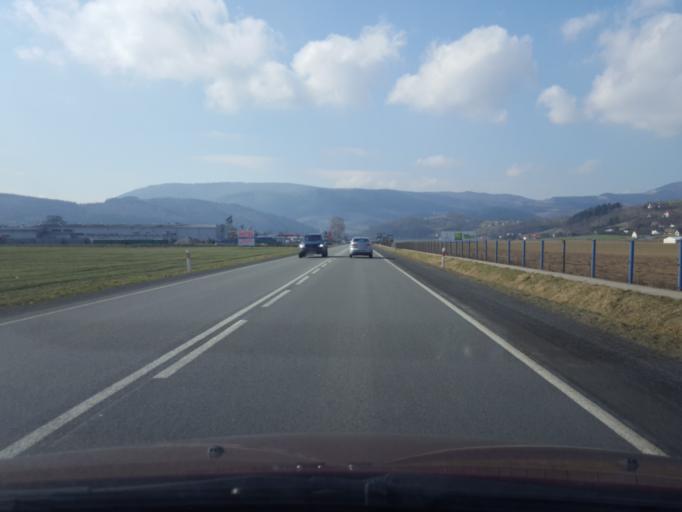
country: PL
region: Lesser Poland Voivodeship
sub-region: Powiat nowosadecki
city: Lososina Dolna
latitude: 49.7480
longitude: 20.6301
